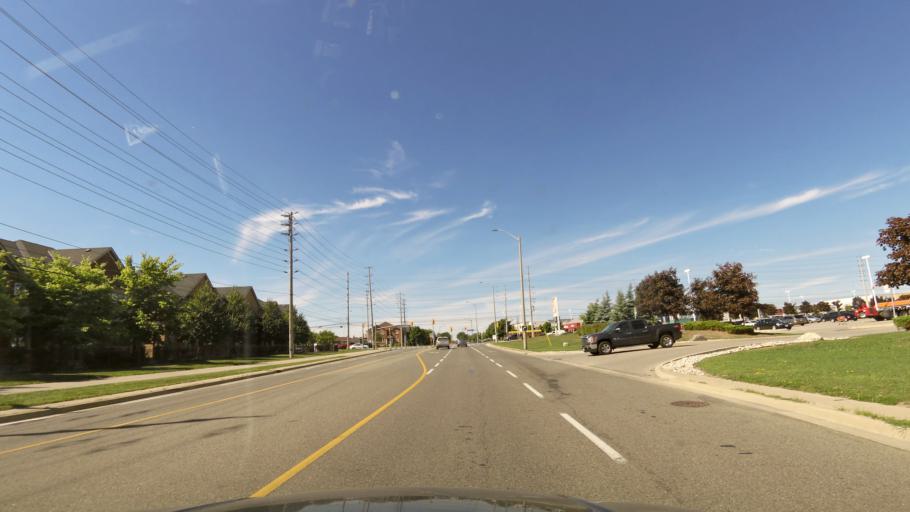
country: CA
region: Ontario
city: Mississauga
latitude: 43.6065
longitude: -79.6999
